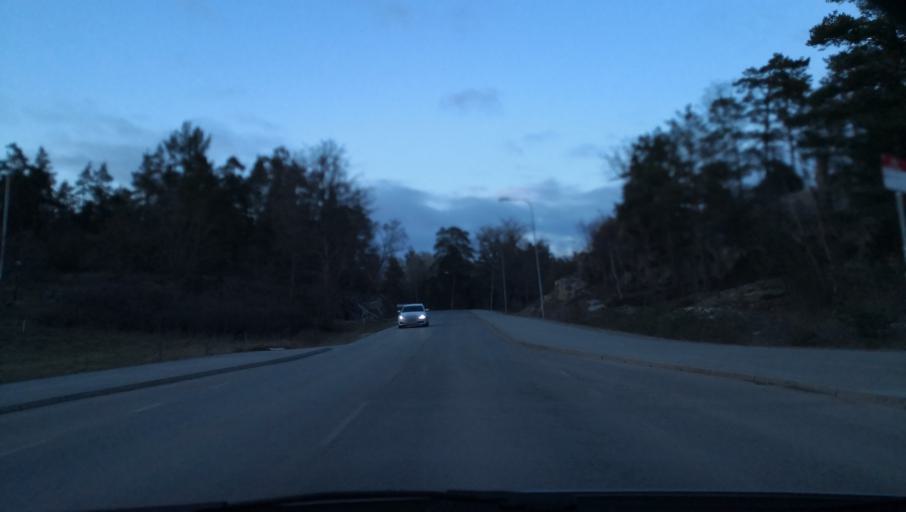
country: SE
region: Stockholm
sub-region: Nacka Kommun
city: Boo
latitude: 59.3387
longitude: 18.2963
